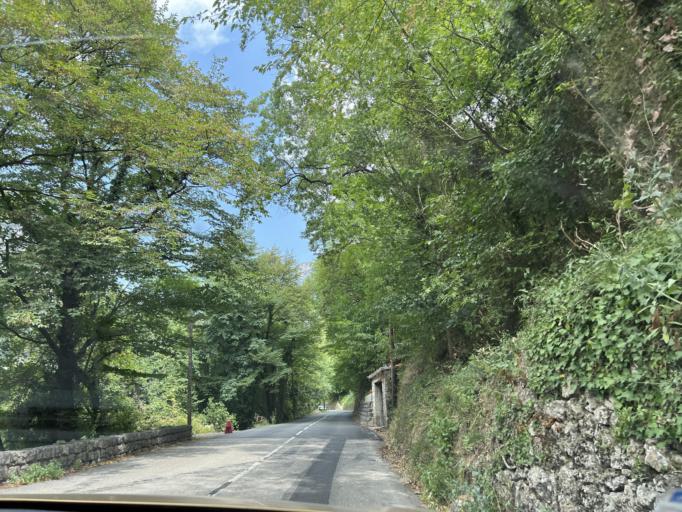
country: FR
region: Provence-Alpes-Cote d'Azur
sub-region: Departement des Alpes-Maritimes
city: Le Rouret
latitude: 43.7218
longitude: 6.9938
